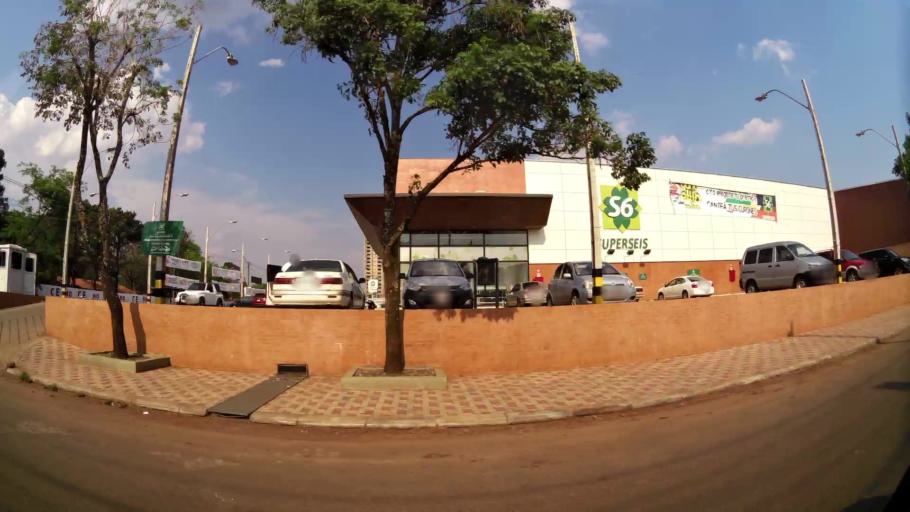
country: PY
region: Alto Parana
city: Presidente Franco
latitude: -25.5257
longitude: -54.6137
